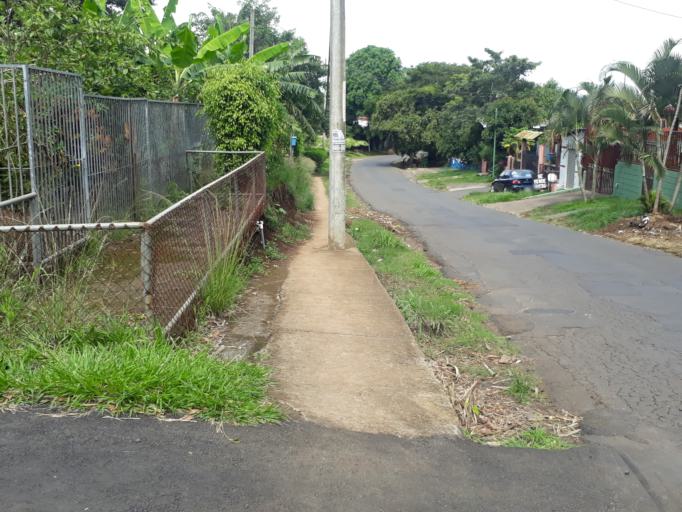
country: CR
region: Alajuela
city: Carrillos
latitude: 10.0255
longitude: -84.3311
